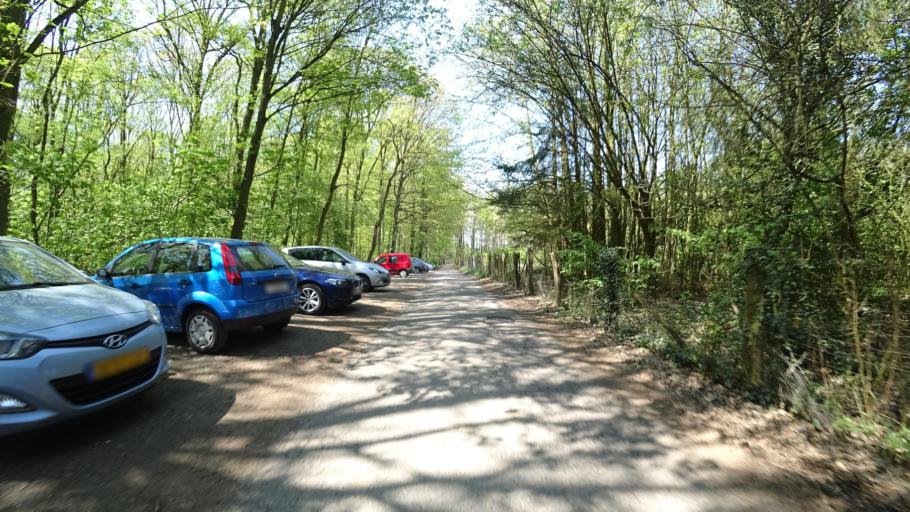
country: BE
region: Wallonia
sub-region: Province du Brabant Wallon
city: Braine-le-Chateau
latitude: 50.7107
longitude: 4.2946
